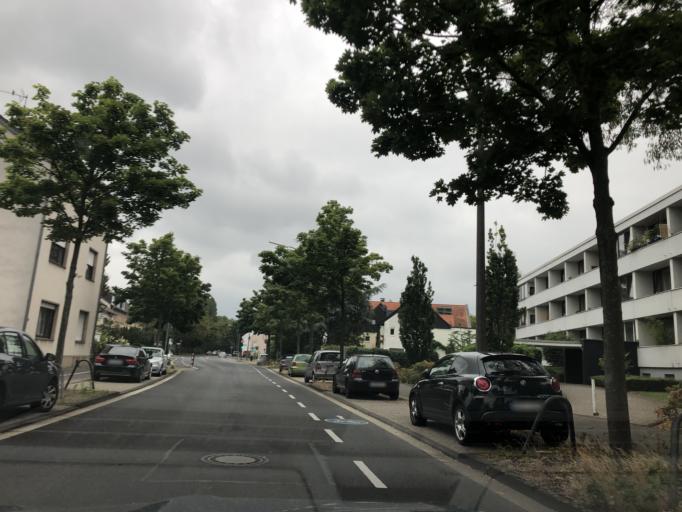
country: DE
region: North Rhine-Westphalia
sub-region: Regierungsbezirk Koln
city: Bonn
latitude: 50.7351
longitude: 7.1240
